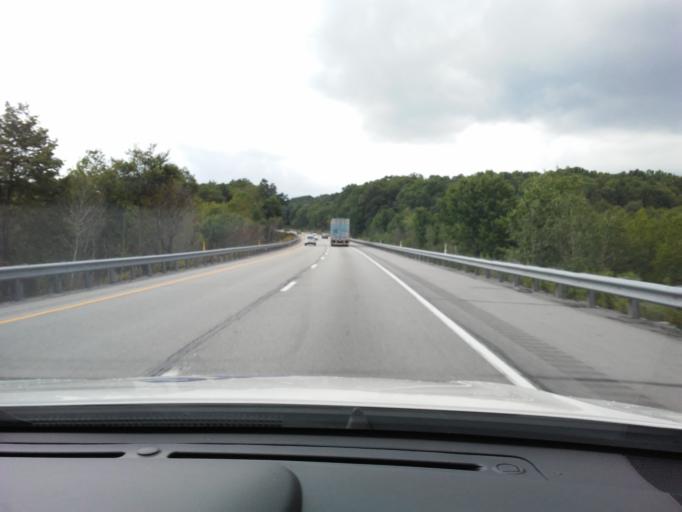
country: US
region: Pennsylvania
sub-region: Clearfield County
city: Troy
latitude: 40.9967
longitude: -78.2192
